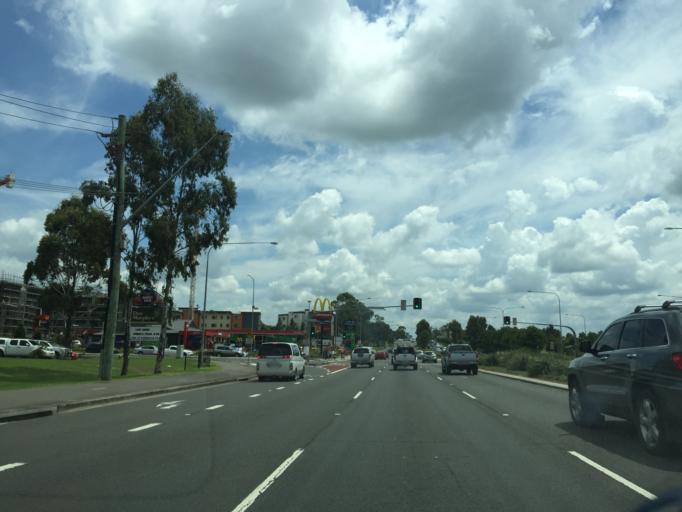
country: AU
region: New South Wales
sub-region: The Hills Shire
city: Beaumont Hills
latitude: -33.7009
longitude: 150.9289
